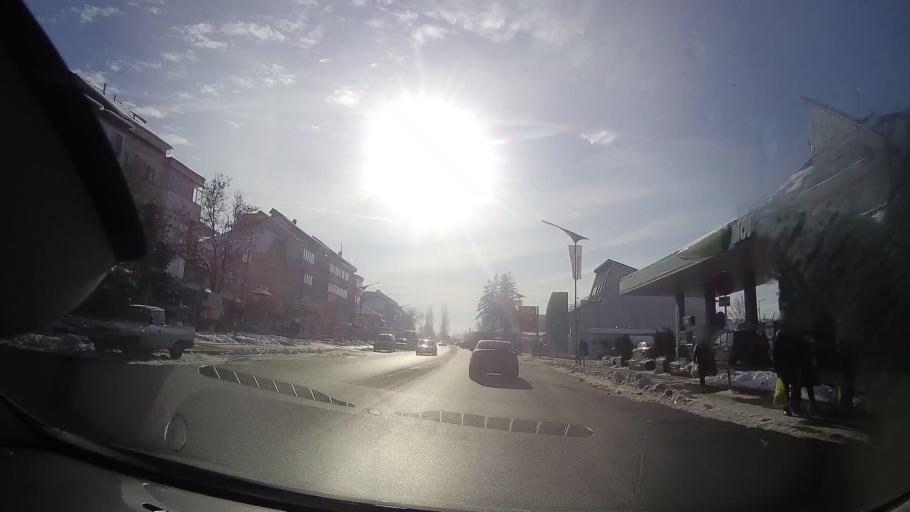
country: RO
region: Neamt
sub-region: Oras Targu Neamt
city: Humulesti
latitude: 47.2042
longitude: 26.3586
